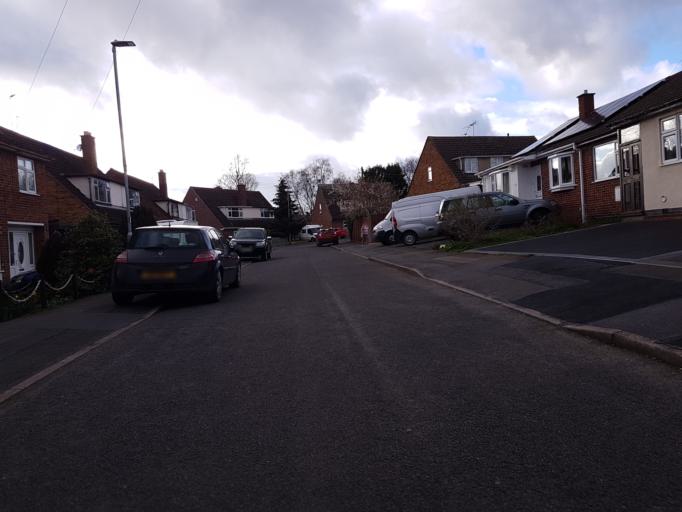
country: GB
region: England
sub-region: Leicestershire
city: Earl Shilton
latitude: 52.5679
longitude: -1.3226
